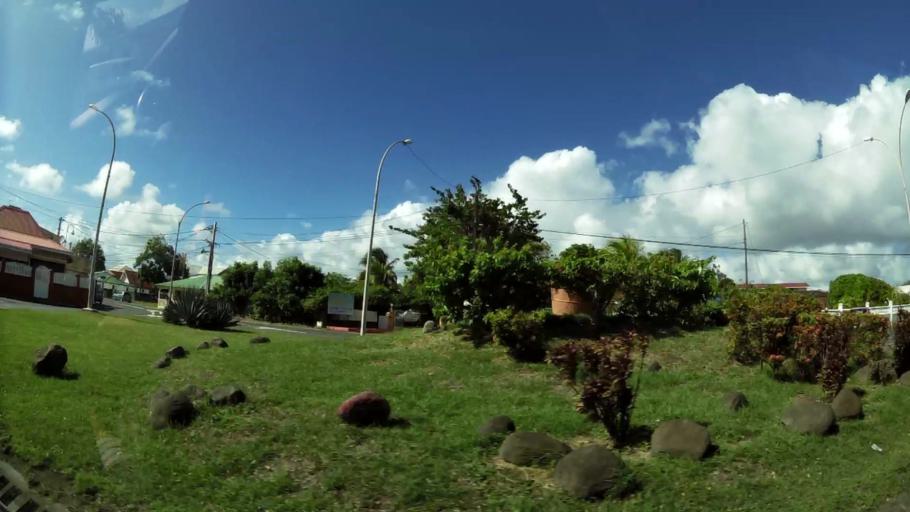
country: GP
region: Guadeloupe
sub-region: Guadeloupe
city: Sainte-Anne
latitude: 16.2262
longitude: -61.3772
